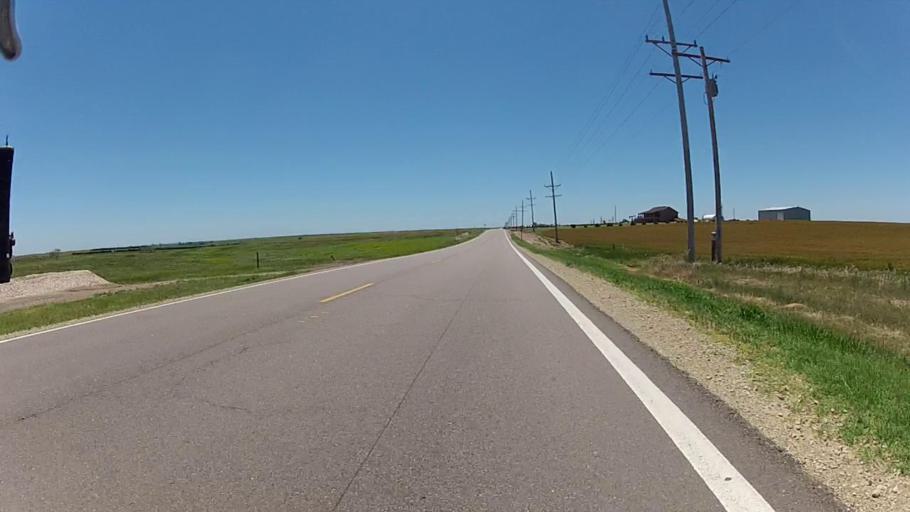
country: US
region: Kansas
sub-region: Kiowa County
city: Greensburg
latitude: 37.5048
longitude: -99.3202
